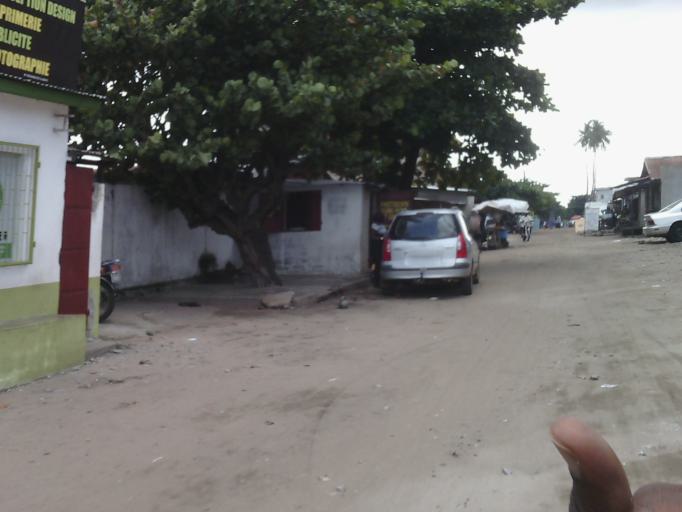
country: BJ
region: Littoral
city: Cotonou
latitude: 6.3652
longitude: 2.4085
